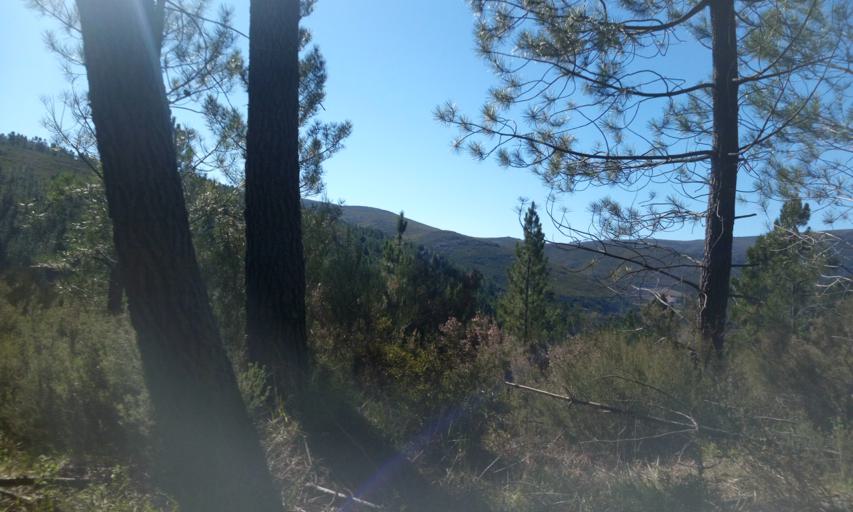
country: PT
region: Guarda
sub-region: Manteigas
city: Manteigas
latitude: 40.4441
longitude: -7.5071
